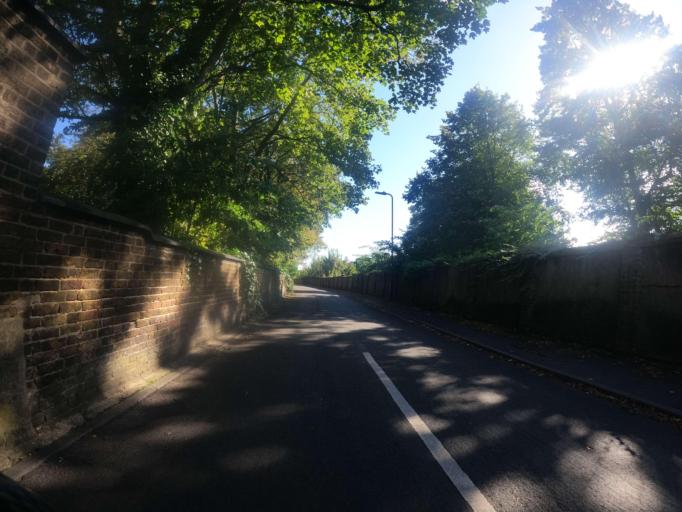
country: GB
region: England
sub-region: Greater London
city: Brentford
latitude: 51.4962
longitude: -0.3052
